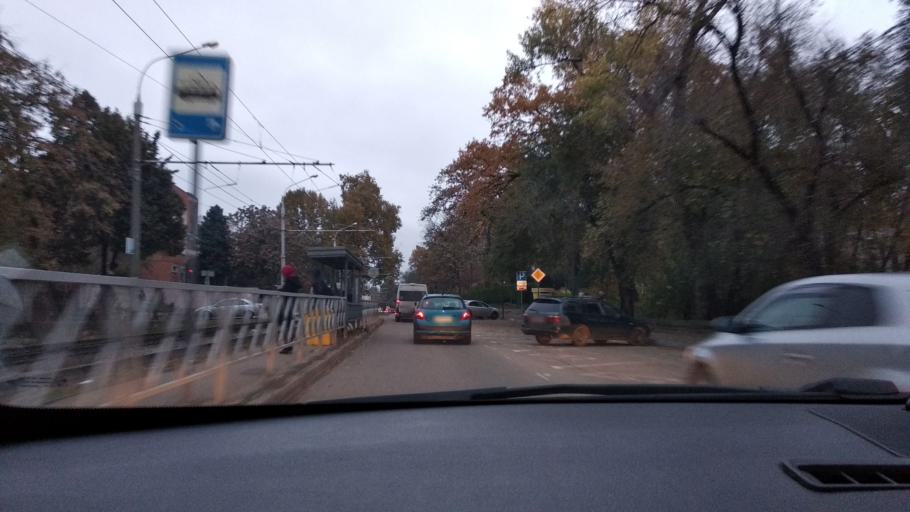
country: RU
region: Adygeya
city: Yablonovskiy
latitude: 45.0096
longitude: 38.9686
